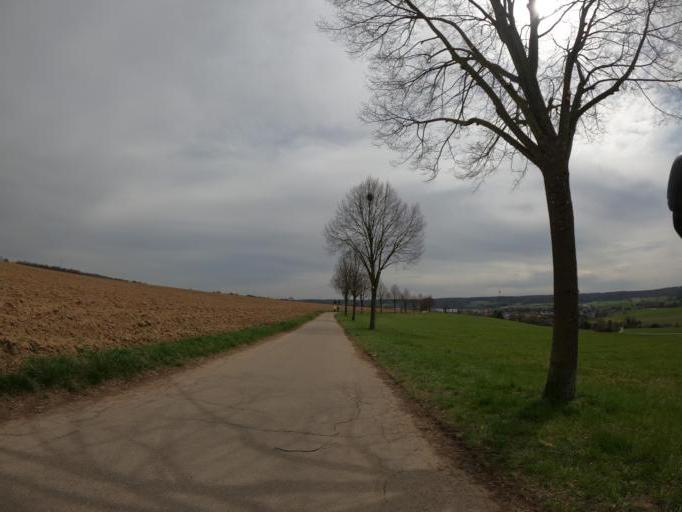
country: DE
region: Baden-Wuerttemberg
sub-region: Regierungsbezirk Stuttgart
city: Waldenbuch
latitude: 48.6520
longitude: 9.1334
